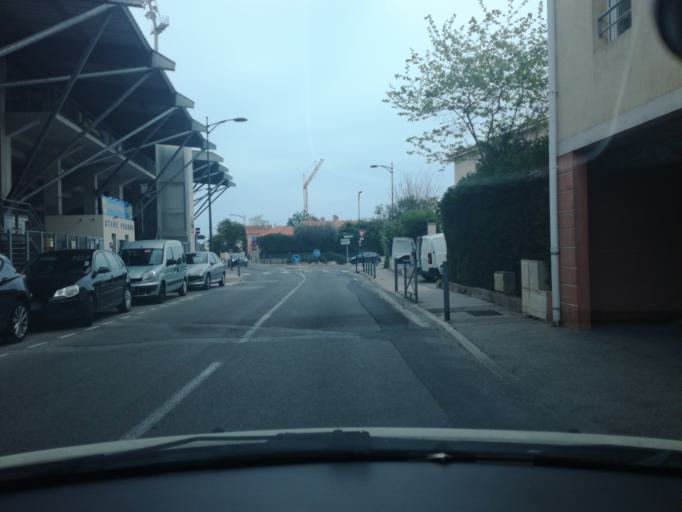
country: FR
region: Provence-Alpes-Cote d'Azur
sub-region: Departement du Var
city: Hyeres
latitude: 43.1198
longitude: 6.1413
